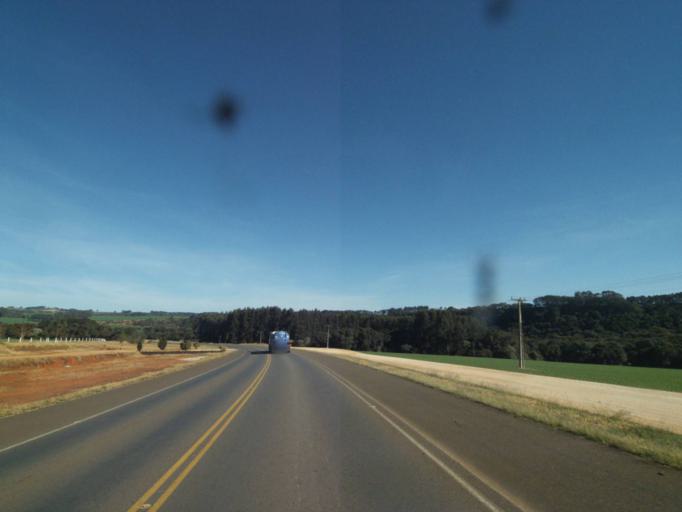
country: BR
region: Parana
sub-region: Tibagi
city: Tibagi
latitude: -24.4720
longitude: -50.4450
